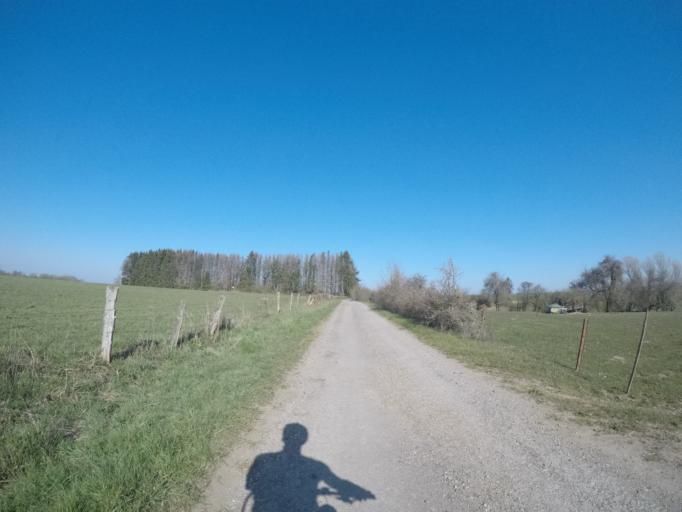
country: BE
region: Wallonia
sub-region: Province du Luxembourg
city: Etalle
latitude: 49.7109
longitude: 5.5761
